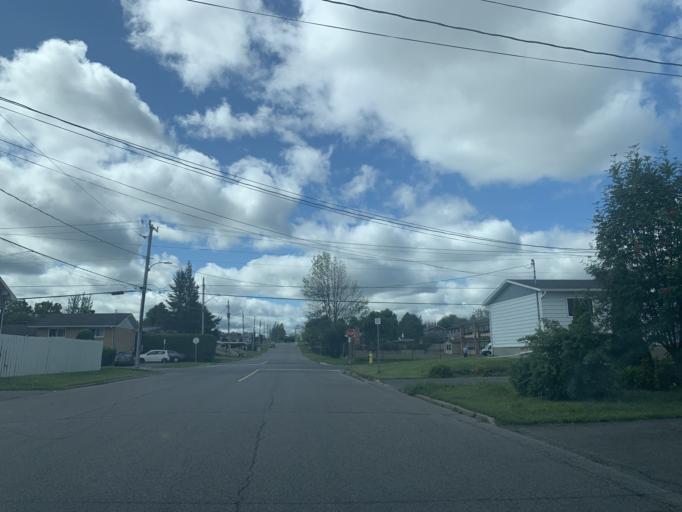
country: CA
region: Ontario
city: Hawkesbury
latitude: 45.6063
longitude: -74.5886
